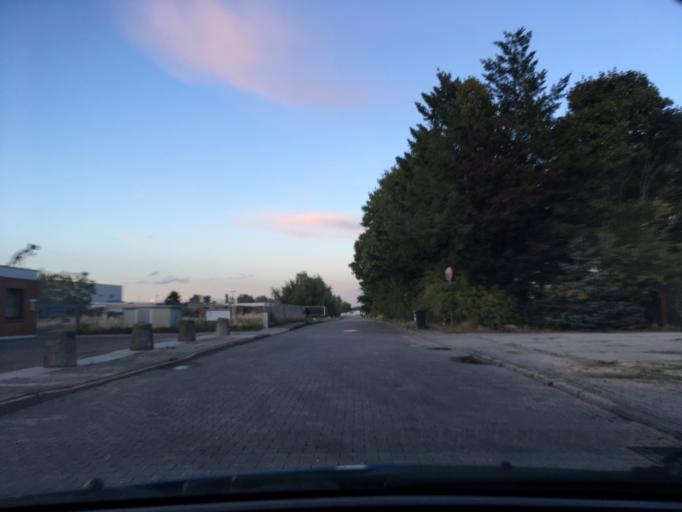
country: DE
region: Schleswig-Holstein
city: Buchhorst
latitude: 53.3692
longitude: 10.5810
